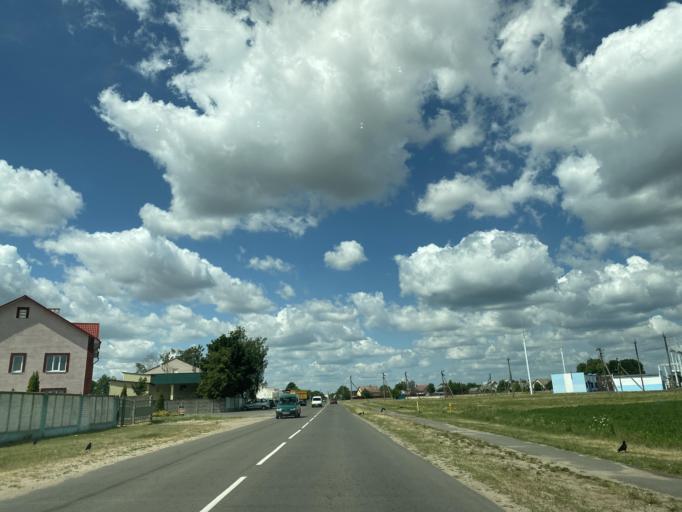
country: BY
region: Brest
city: Ivanava
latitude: 52.1398
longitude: 25.5518
